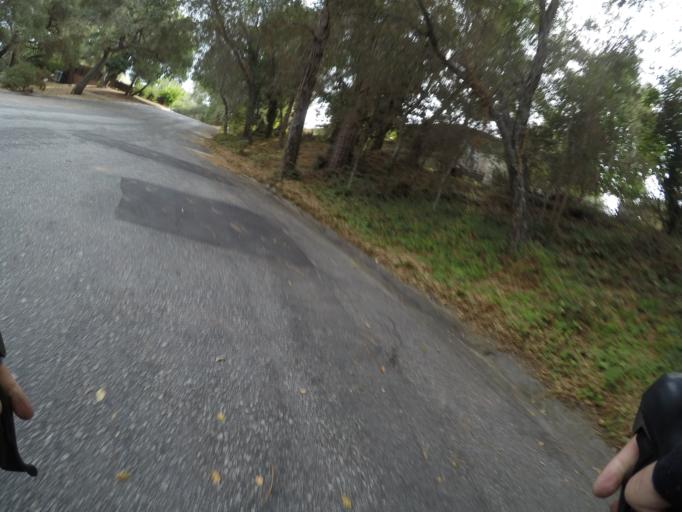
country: US
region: California
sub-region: Santa Cruz County
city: Mount Hermon
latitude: 37.0637
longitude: -122.0636
